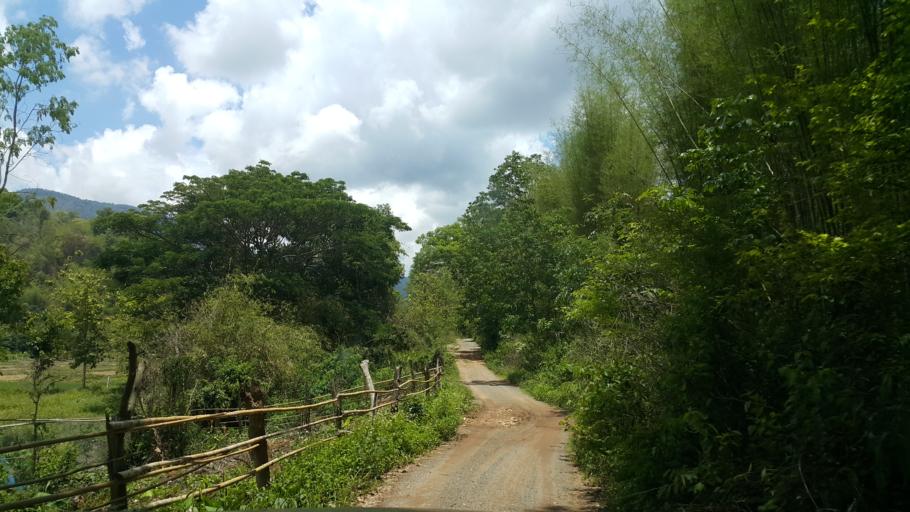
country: TH
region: Phayao
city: Phayao
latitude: 19.1756
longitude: 99.7799
